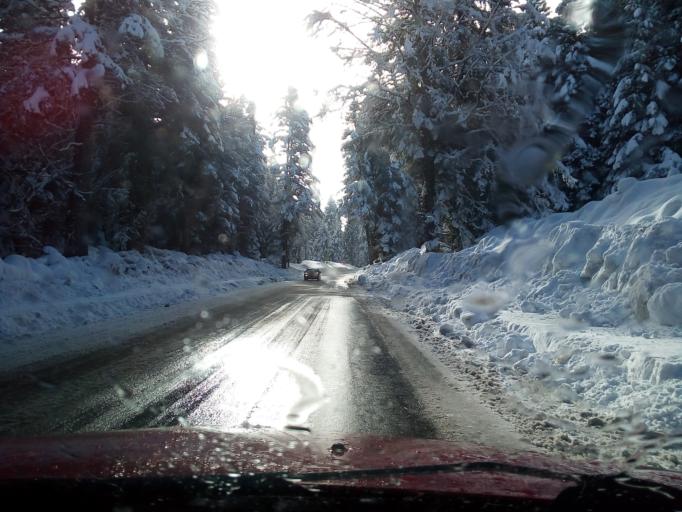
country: FR
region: Rhone-Alpes
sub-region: Departement de l'Isere
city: Le Sappey-en-Chartreuse
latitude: 45.2989
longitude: 5.7697
